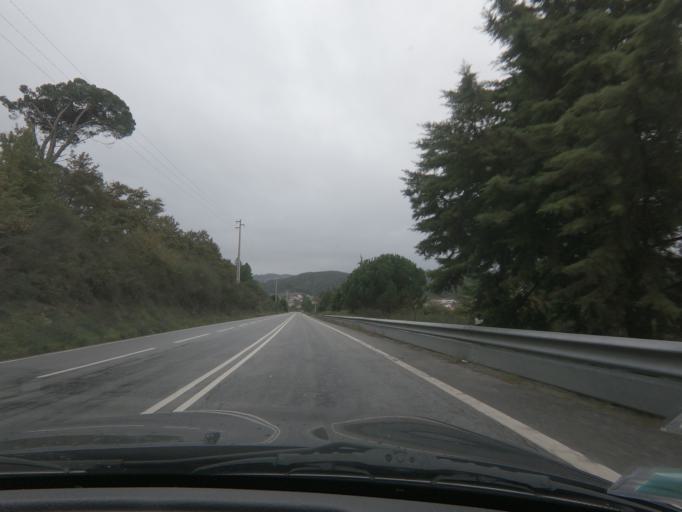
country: PT
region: Porto
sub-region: Amarante
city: Teloes
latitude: 41.2979
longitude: -8.0913
